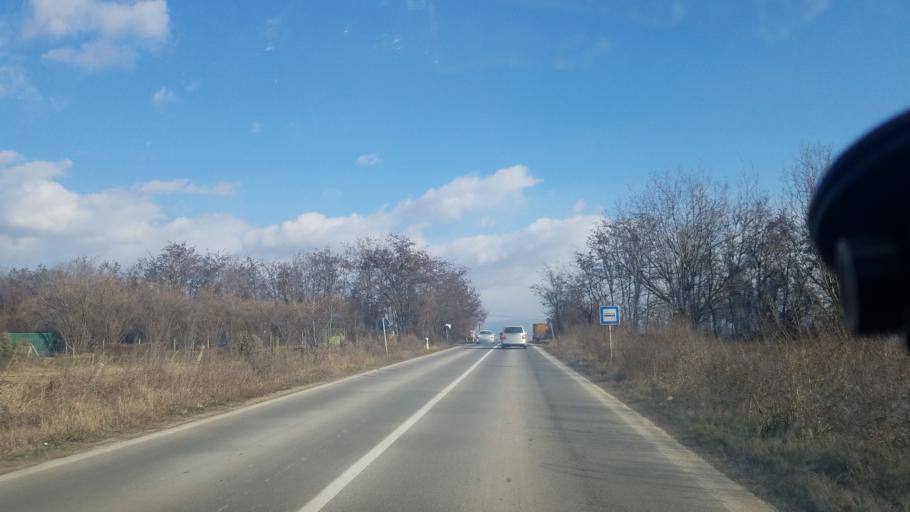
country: MK
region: Kocani
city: Kochani
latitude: 41.8998
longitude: 22.3785
